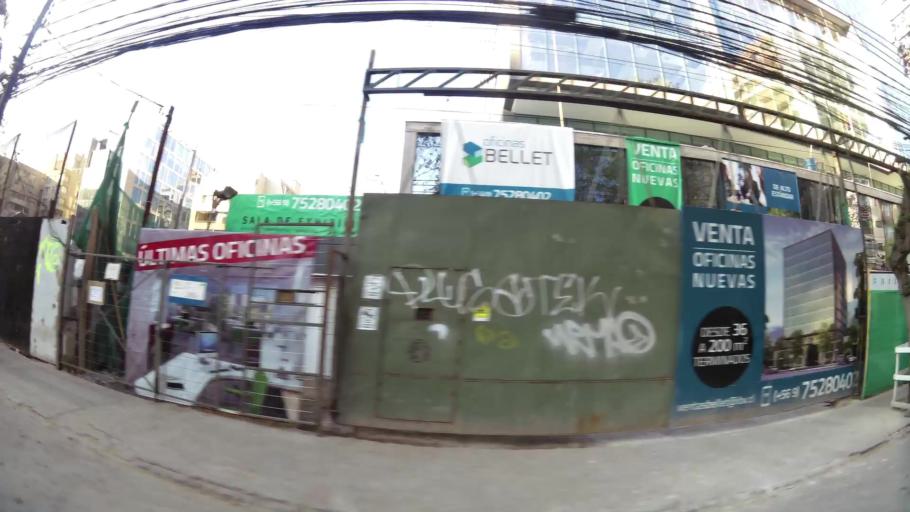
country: CL
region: Santiago Metropolitan
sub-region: Provincia de Santiago
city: Santiago
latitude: -33.4261
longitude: -70.6175
